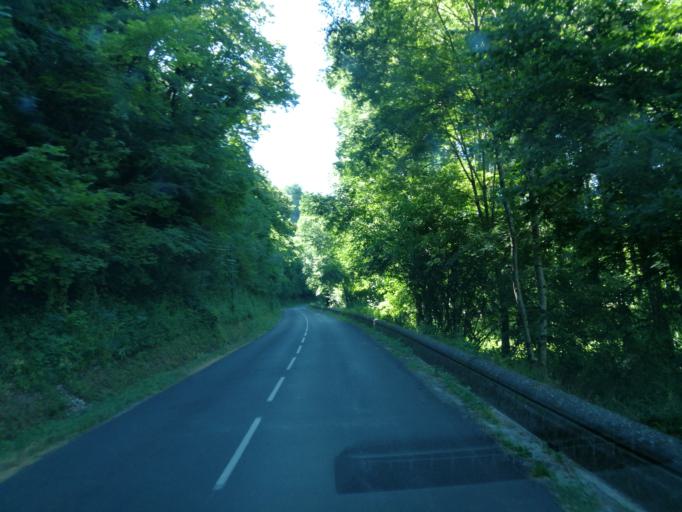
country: FR
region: Midi-Pyrenees
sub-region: Departement du Lot
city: Souillac
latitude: 44.8665
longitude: 1.4229
